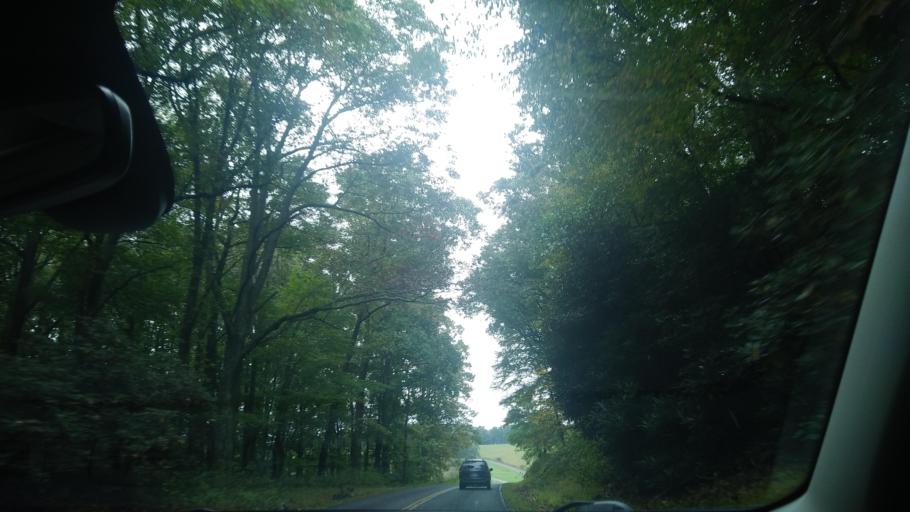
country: US
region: Virginia
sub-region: Carroll County
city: Cana
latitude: 36.6661
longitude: -80.6062
